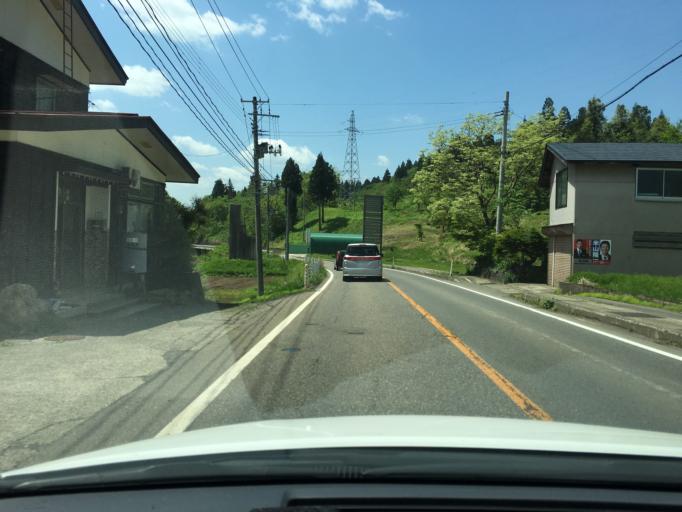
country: JP
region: Niigata
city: Tochio-honcho
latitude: 37.3016
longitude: 138.9965
